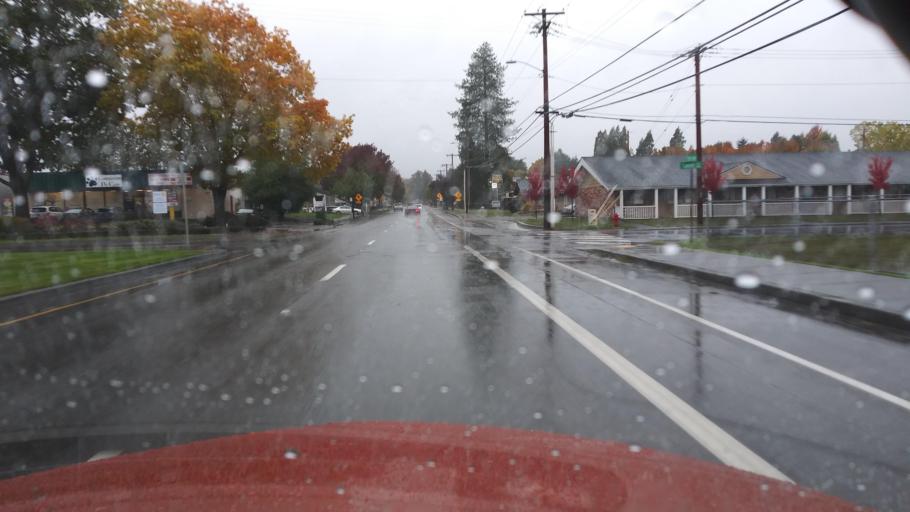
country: US
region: Oregon
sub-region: Washington County
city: Forest Grove
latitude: 45.5202
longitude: -123.0922
